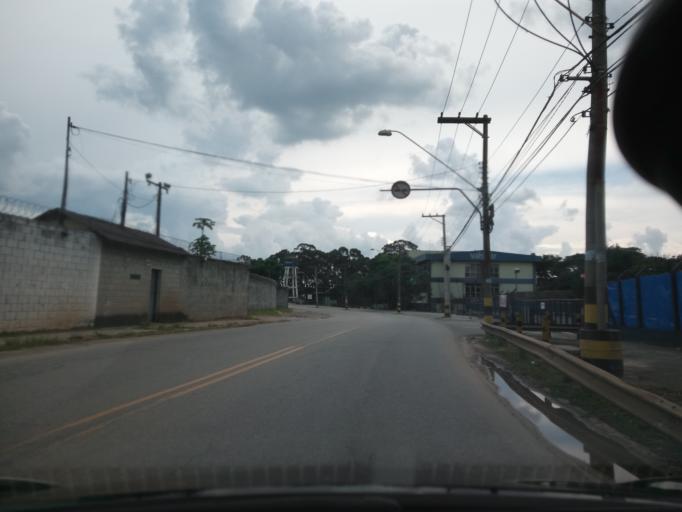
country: BR
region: Sao Paulo
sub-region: Sao Bernardo Do Campo
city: Sao Bernardo do Campo
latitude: -23.7419
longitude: -46.5864
